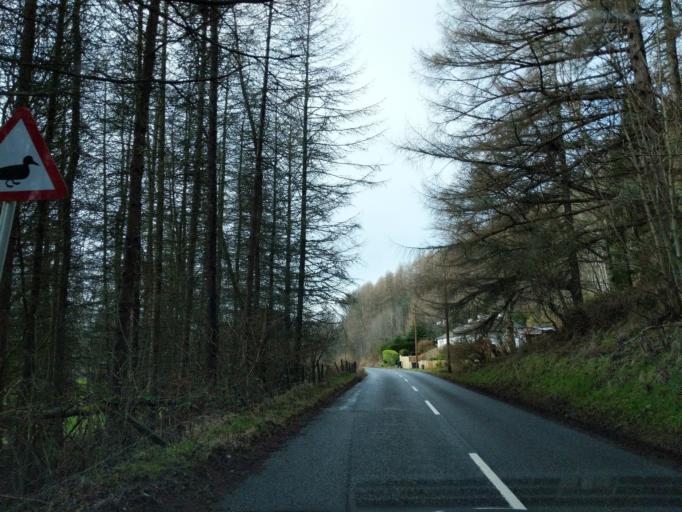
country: GB
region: Scotland
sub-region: Perth and Kinross
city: Aberfeldy
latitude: 56.5830
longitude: -4.0180
